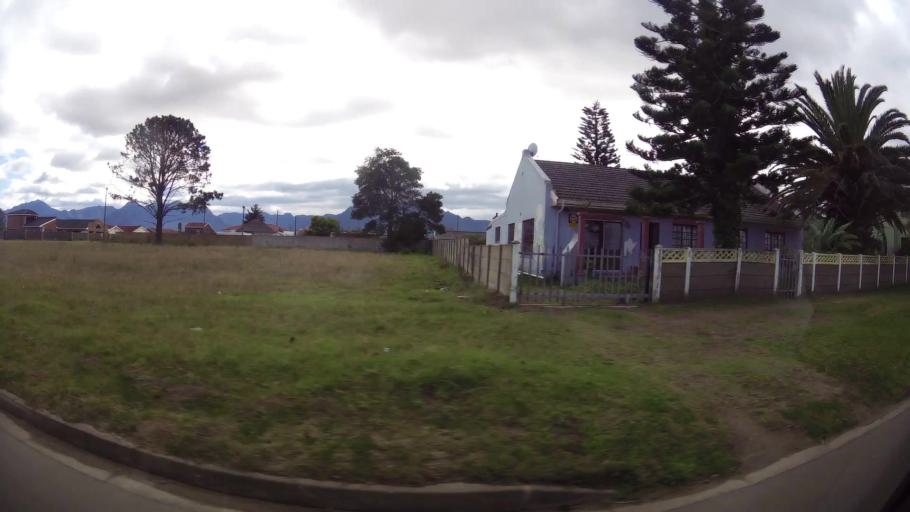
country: ZA
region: Western Cape
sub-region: Eden District Municipality
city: George
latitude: -34.0100
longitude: 22.4397
